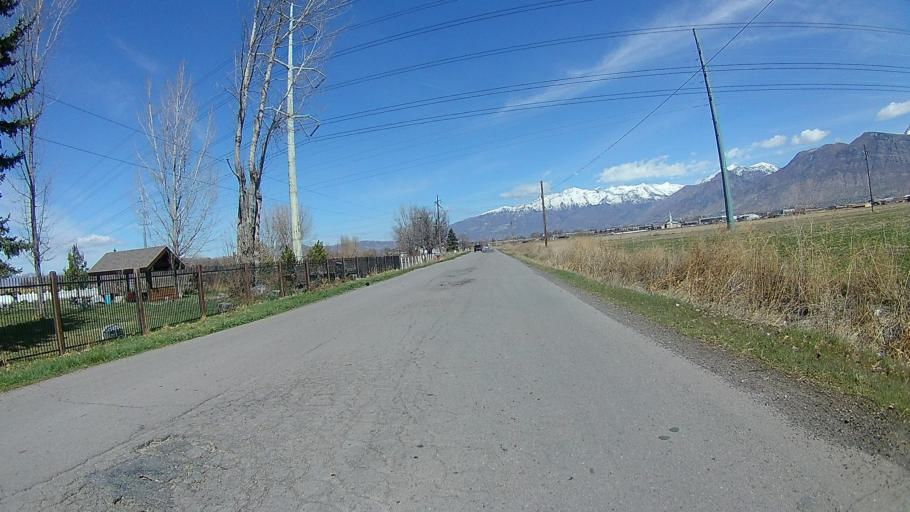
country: US
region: Utah
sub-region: Utah County
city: American Fork
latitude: 40.3501
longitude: -111.7952
